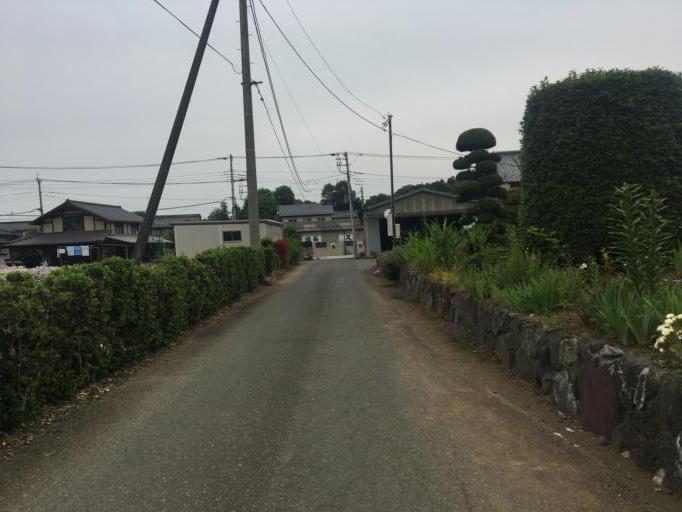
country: JP
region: Saitama
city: Sakado
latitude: 36.0170
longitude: 139.4373
